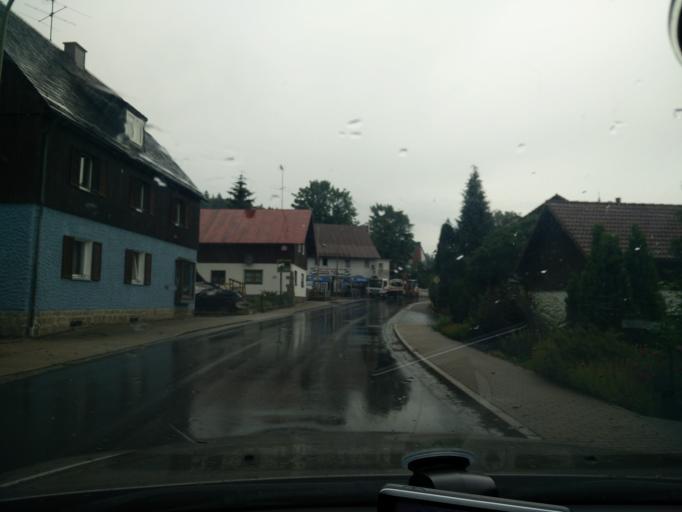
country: DE
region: Bavaria
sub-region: Upper Franconia
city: Fichtelberg
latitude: 49.9980
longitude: 11.8502
